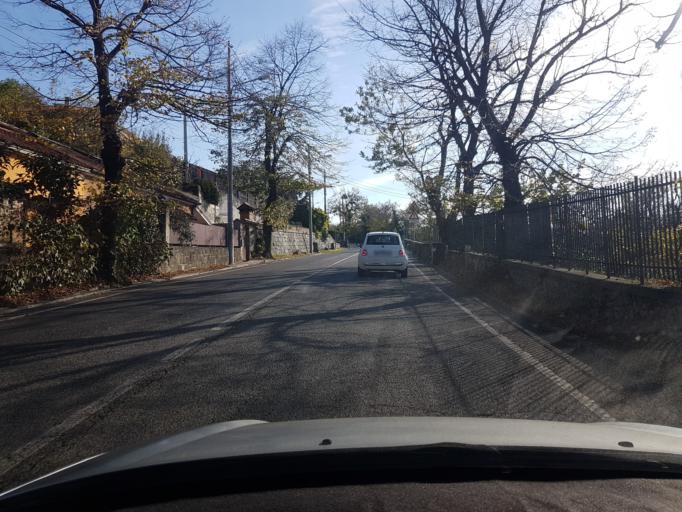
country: IT
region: Friuli Venezia Giulia
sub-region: Provincia di Trieste
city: Trieste
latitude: 45.6542
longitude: 13.8163
